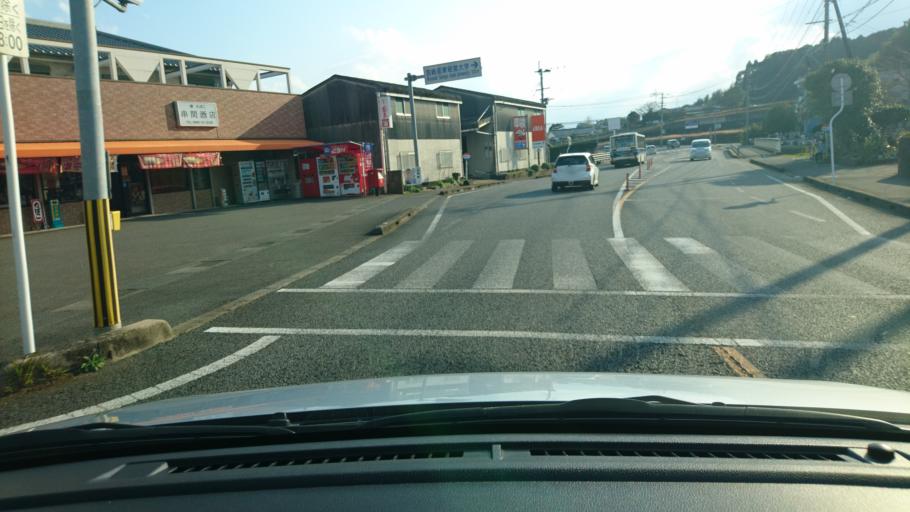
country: JP
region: Miyazaki
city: Miyazaki-shi
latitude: 31.8844
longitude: 131.4089
